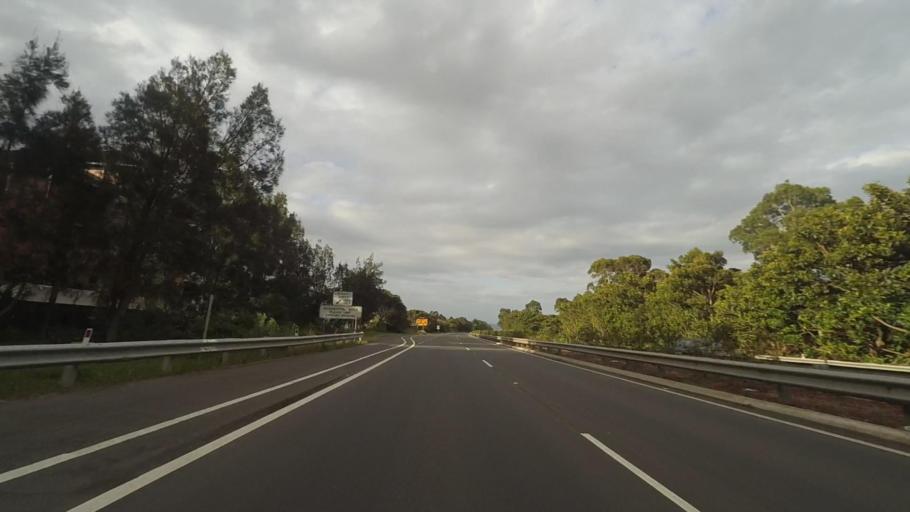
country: AU
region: New South Wales
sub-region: Wollongong
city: Fairy Meadow
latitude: -34.4023
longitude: 150.8930
